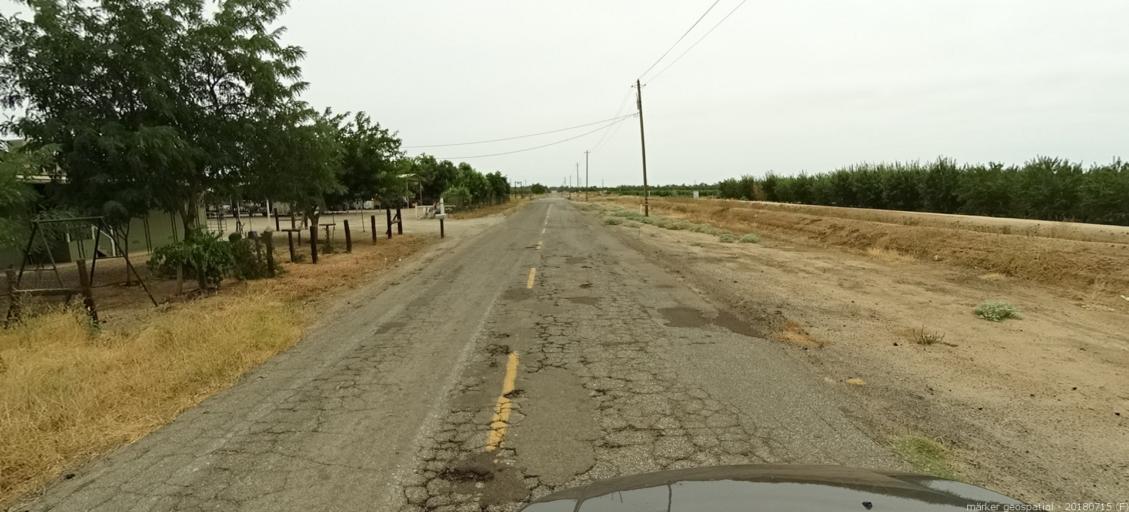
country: US
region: California
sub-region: Madera County
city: Madera Acres
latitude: 37.0255
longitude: -120.1056
